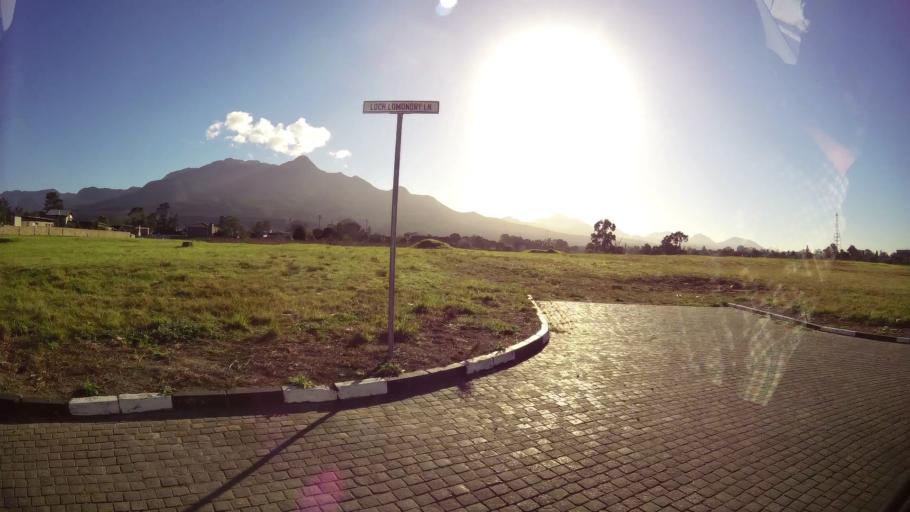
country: ZA
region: Western Cape
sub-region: Eden District Municipality
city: George
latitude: -33.9600
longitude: 22.4445
